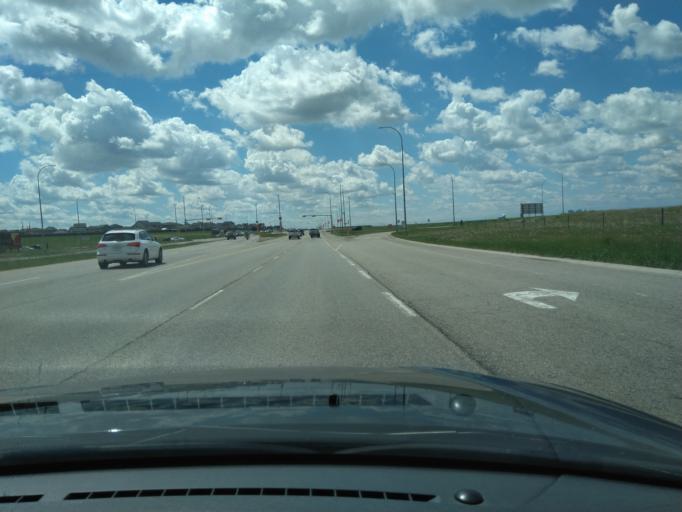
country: CA
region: Alberta
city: Airdrie
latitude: 51.1671
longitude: -113.9703
